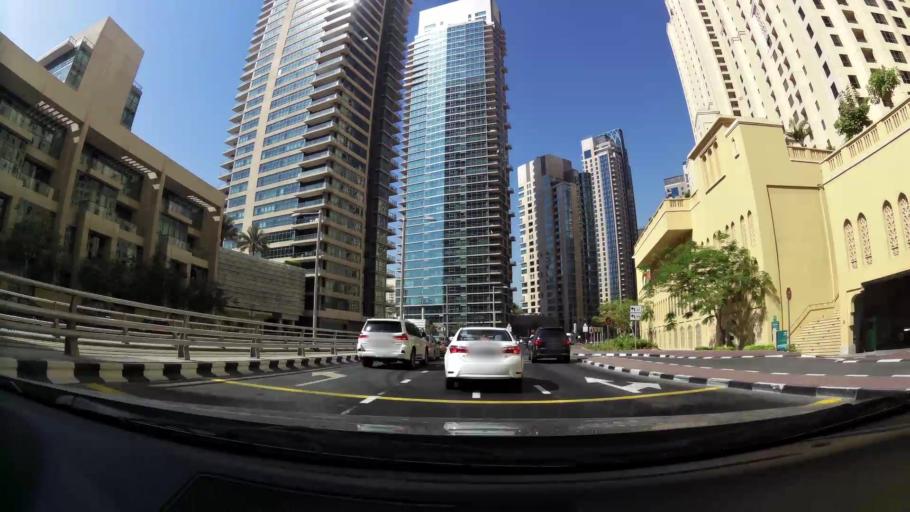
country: AE
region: Dubai
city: Dubai
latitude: 25.0774
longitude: 55.1363
